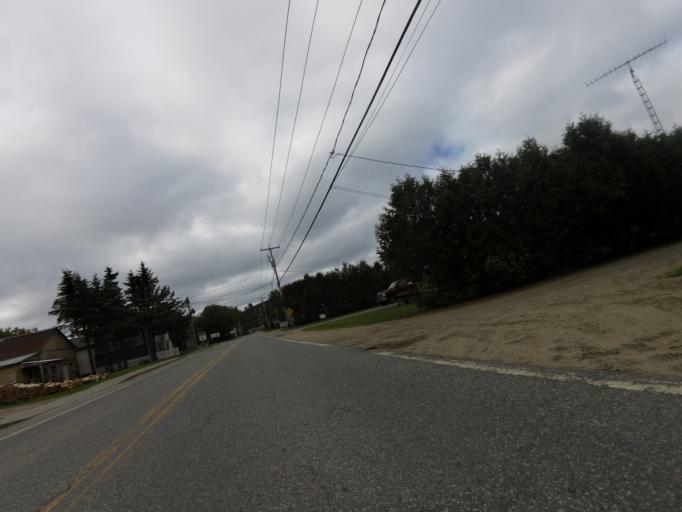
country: CA
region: Quebec
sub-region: Outaouais
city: Shawville
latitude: 45.8522
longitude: -76.4305
